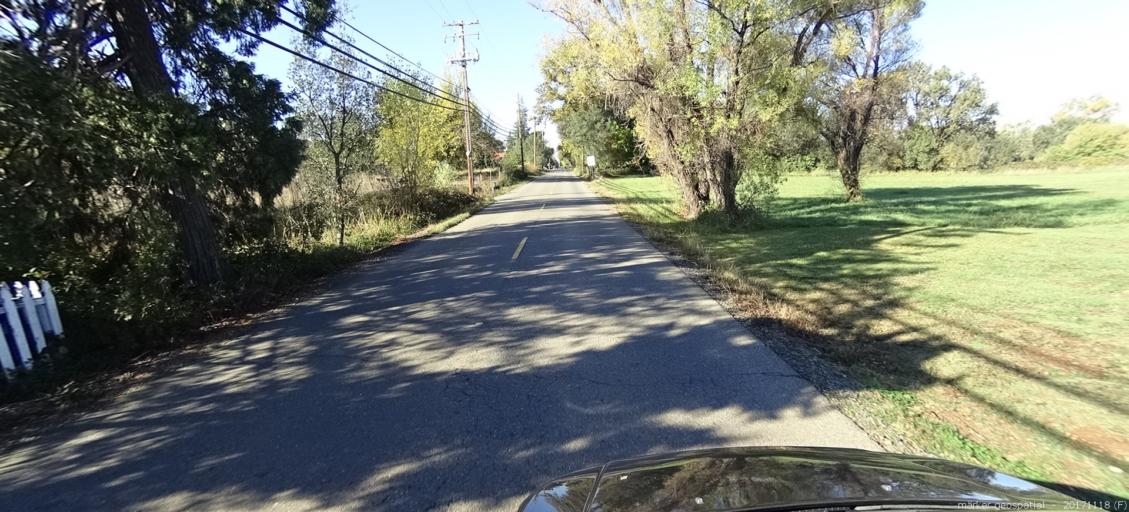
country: US
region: California
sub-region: Shasta County
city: Cottonwood
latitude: 40.3857
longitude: -122.3014
